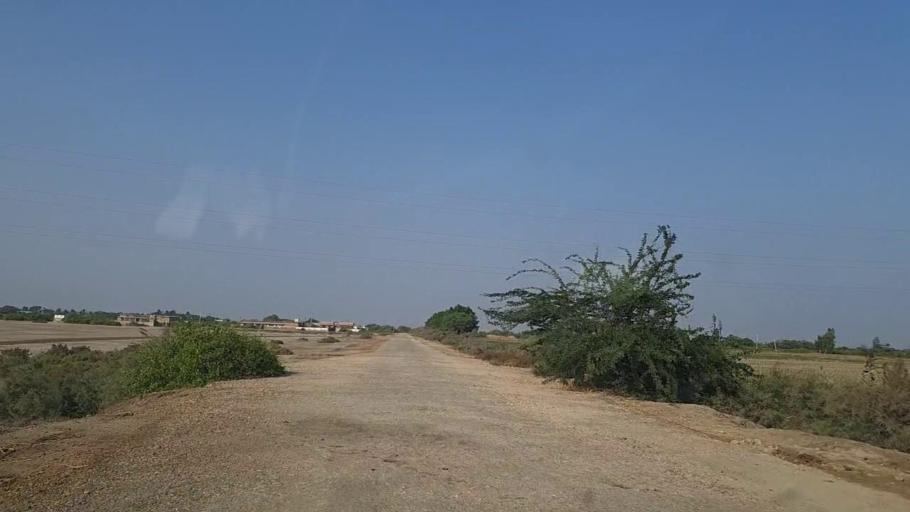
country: PK
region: Sindh
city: Mirpur Sakro
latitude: 24.5661
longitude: 67.6857
